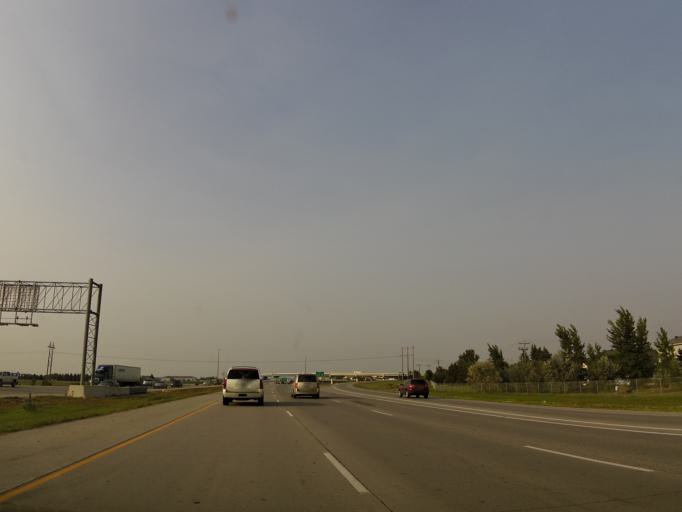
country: US
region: North Dakota
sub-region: Cass County
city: Fargo
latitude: 46.8413
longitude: -96.8408
